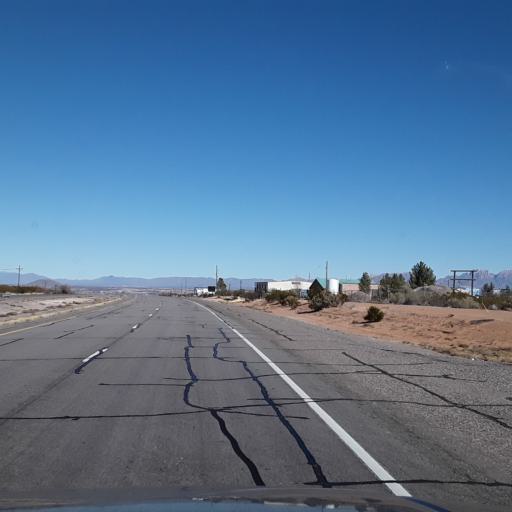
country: US
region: New Mexico
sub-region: Dona Ana County
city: Mesilla
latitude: 32.2853
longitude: -106.8774
